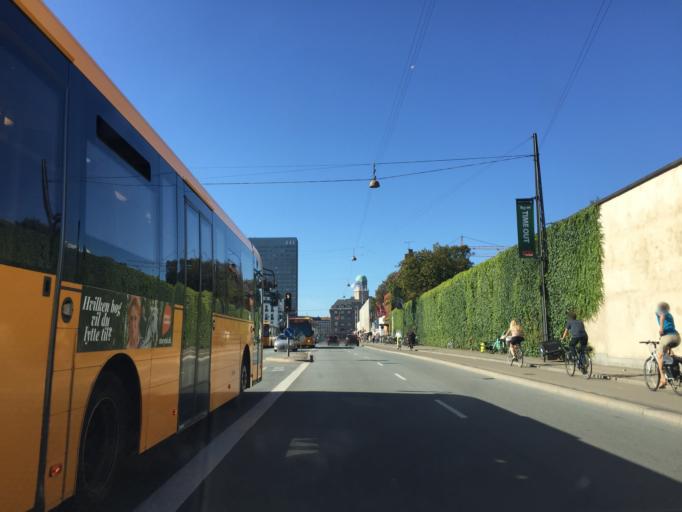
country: DK
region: Capital Region
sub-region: Kobenhavn
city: Copenhagen
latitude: 55.6719
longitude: 12.5675
